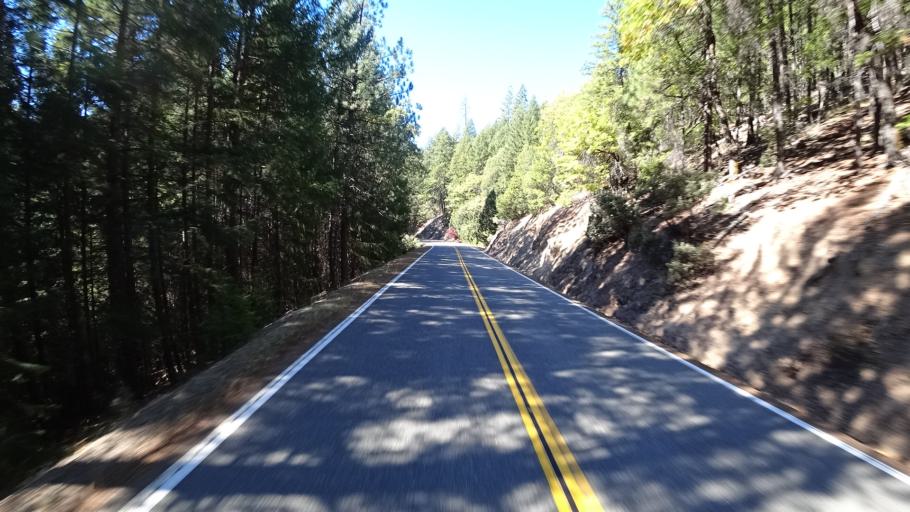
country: US
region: California
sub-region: Trinity County
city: Weaverville
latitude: 41.2093
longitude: -123.0589
